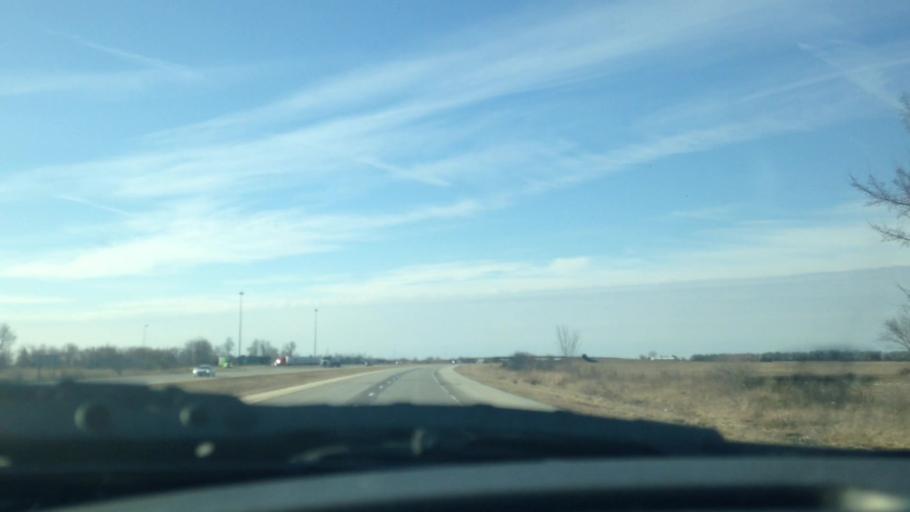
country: US
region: Illinois
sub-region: Ford County
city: Paxton
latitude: 40.5512
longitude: -88.0608
